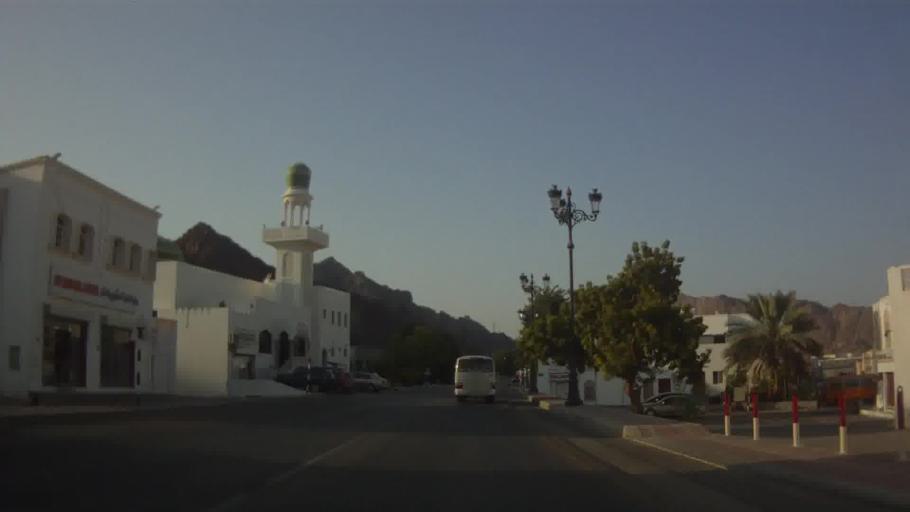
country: OM
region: Muhafazat Masqat
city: Muscat
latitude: 23.5958
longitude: 58.5976
